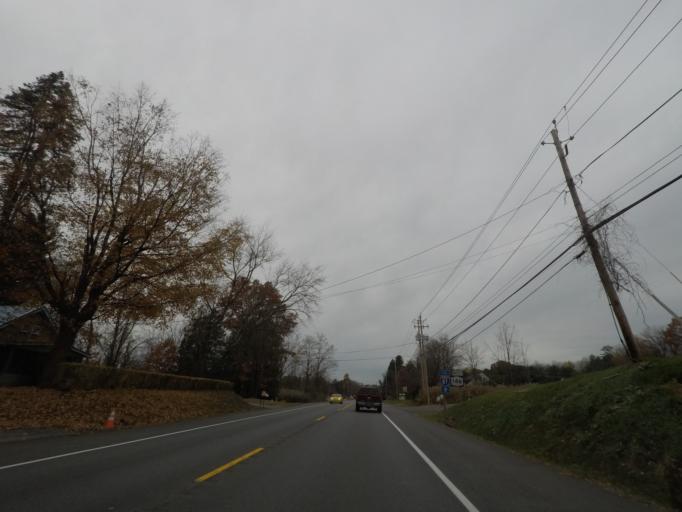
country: US
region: New York
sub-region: Saratoga County
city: Mechanicville
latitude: 42.8644
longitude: -73.7492
